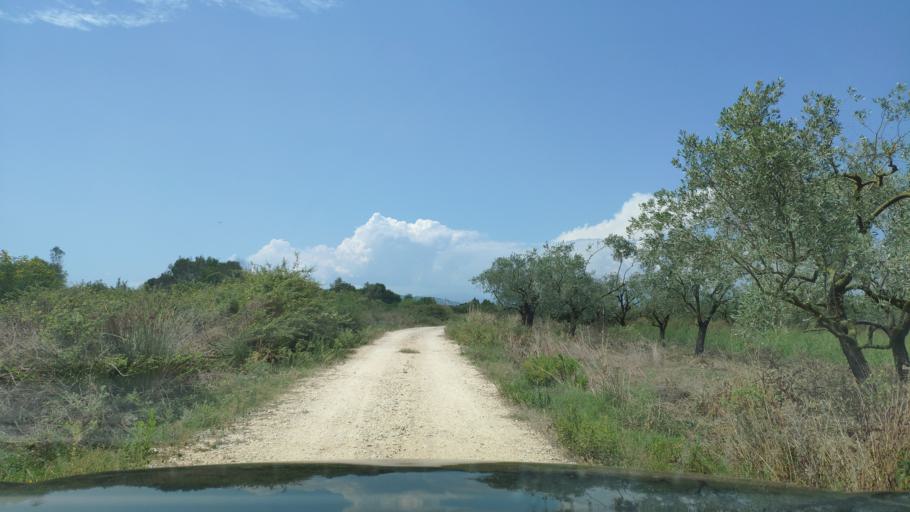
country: GR
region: West Greece
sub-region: Nomos Aitolias kai Akarnanias
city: Menidi
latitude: 39.0552
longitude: 21.0960
